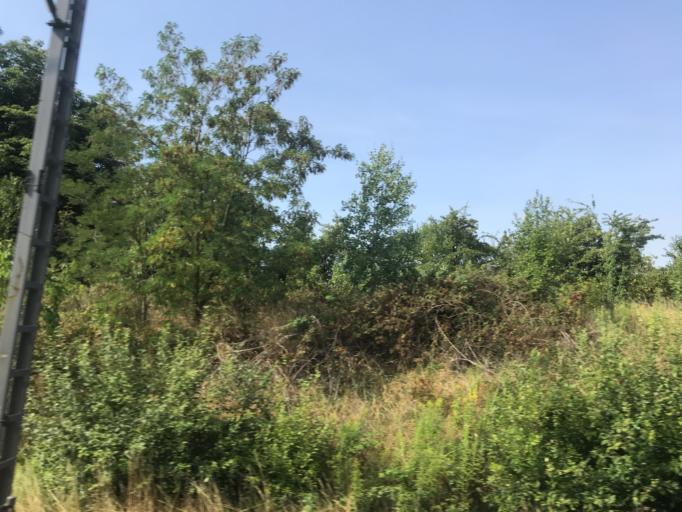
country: CZ
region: Central Bohemia
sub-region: Okres Praha-Vychod
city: Strancice
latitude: 49.9559
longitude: 14.6563
